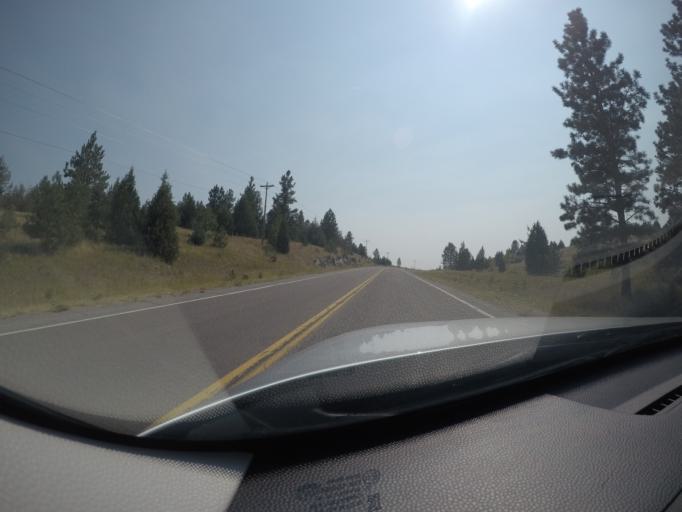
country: US
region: Montana
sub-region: Lake County
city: Polson
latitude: 47.7467
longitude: -114.1725
